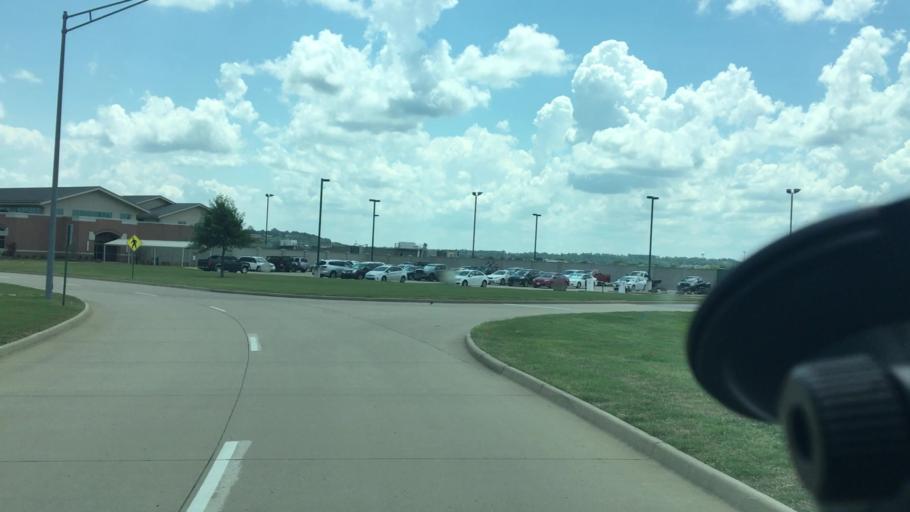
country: US
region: Arkansas
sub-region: Sebastian County
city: Fort Smith
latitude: 35.3413
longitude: -94.3606
